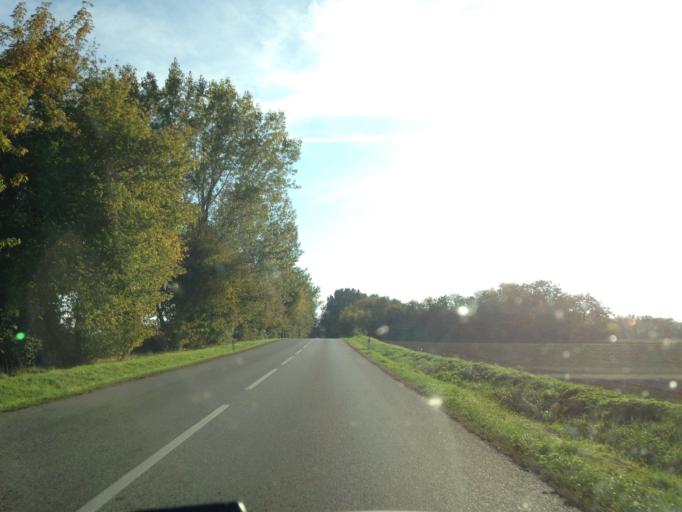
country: SK
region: Nitriansky
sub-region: Okres Komarno
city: Hurbanovo
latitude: 47.8179
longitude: 18.2249
